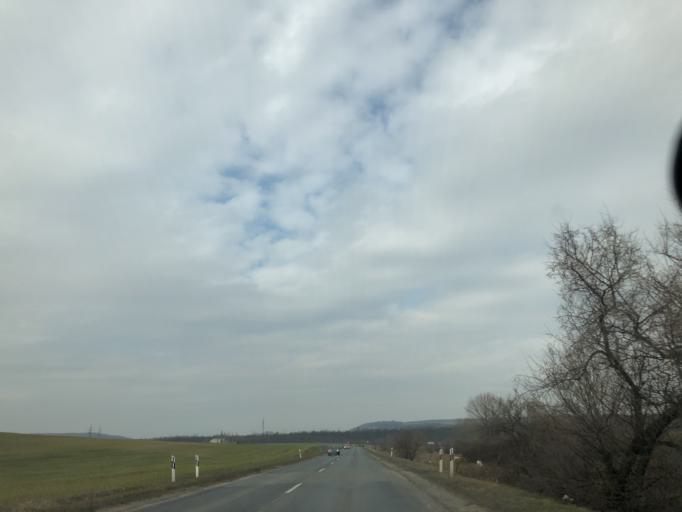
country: HU
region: Fejer
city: Bicske
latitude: 47.4751
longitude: 18.5763
